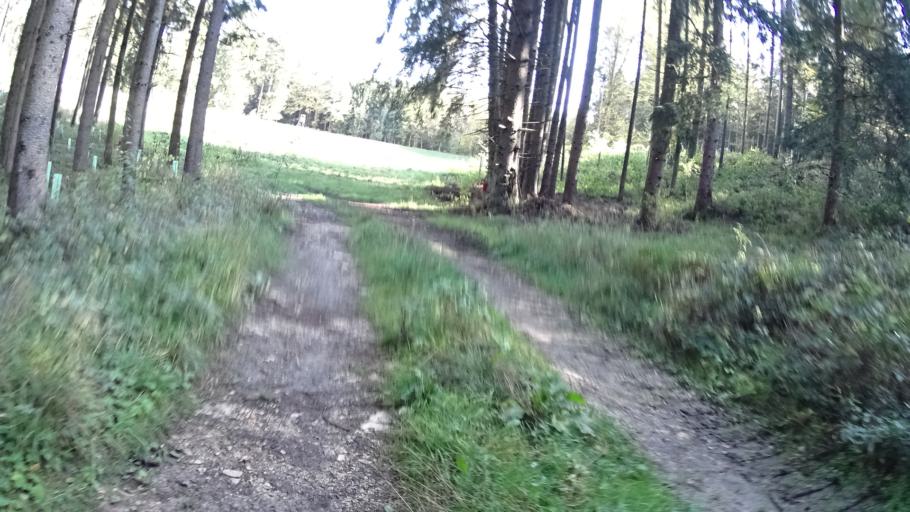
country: DE
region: Bavaria
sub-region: Upper Bavaria
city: Bohmfeld
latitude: 48.8775
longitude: 11.3686
